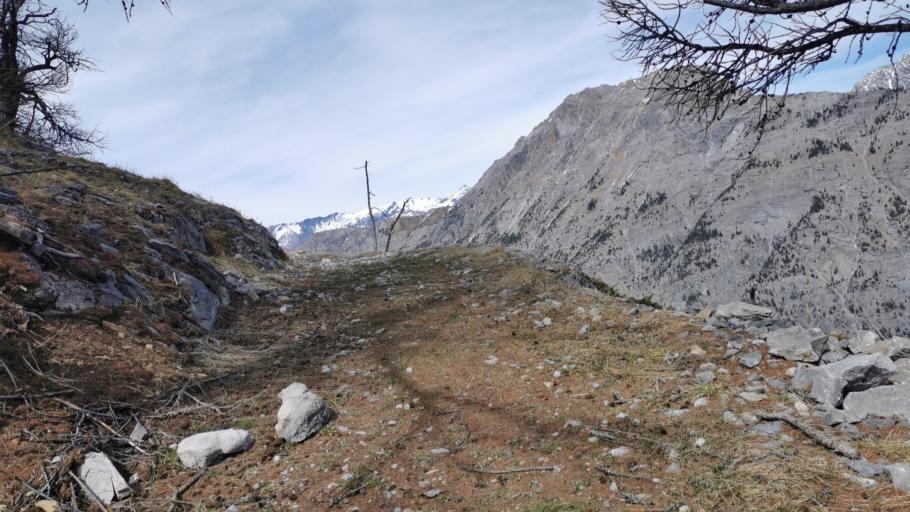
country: FR
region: Provence-Alpes-Cote d'Azur
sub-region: Departement des Hautes-Alpes
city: Saint-Chaffrey
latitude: 44.9976
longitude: 6.6487
